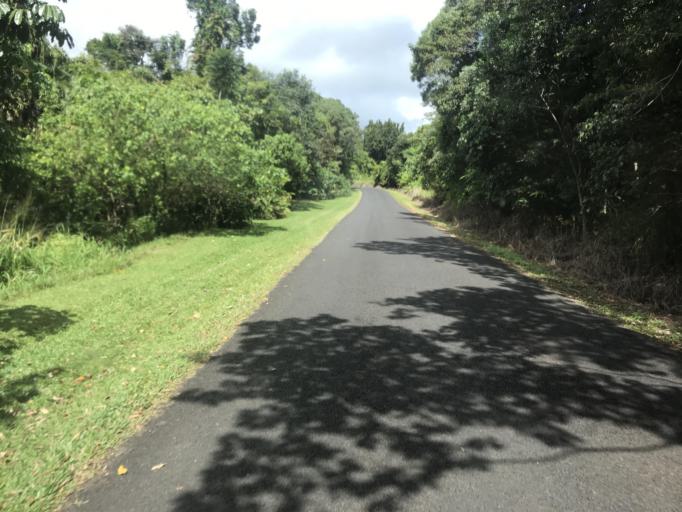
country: AU
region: Queensland
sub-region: Cassowary Coast
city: Innisfail
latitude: -17.5502
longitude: 145.8648
